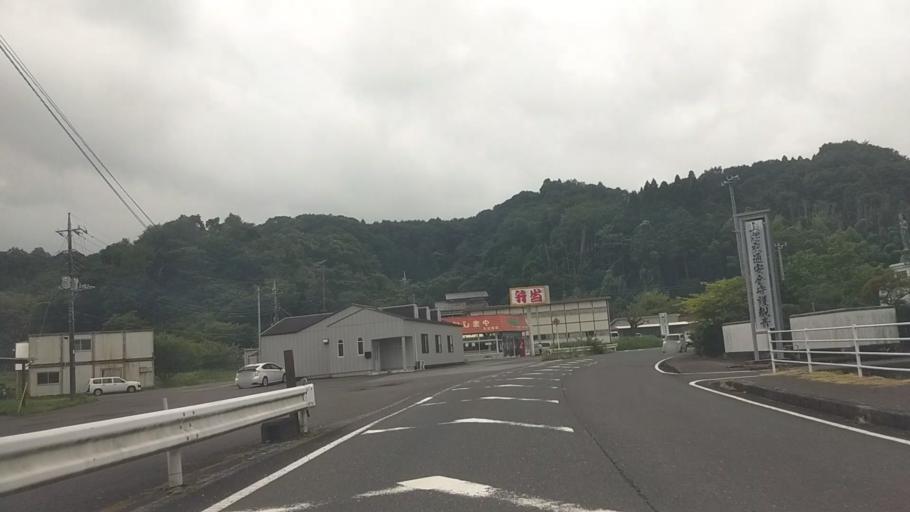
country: JP
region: Chiba
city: Kisarazu
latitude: 35.2867
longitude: 140.0831
